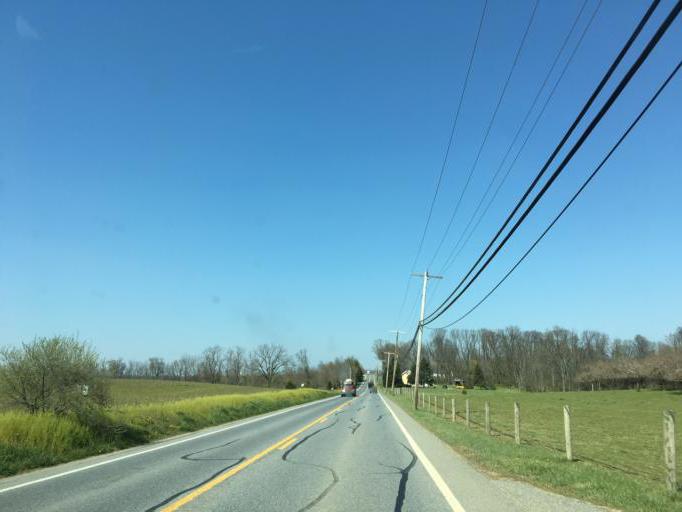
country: US
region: Maryland
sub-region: Carroll County
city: New Windsor
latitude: 39.5206
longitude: -77.1065
